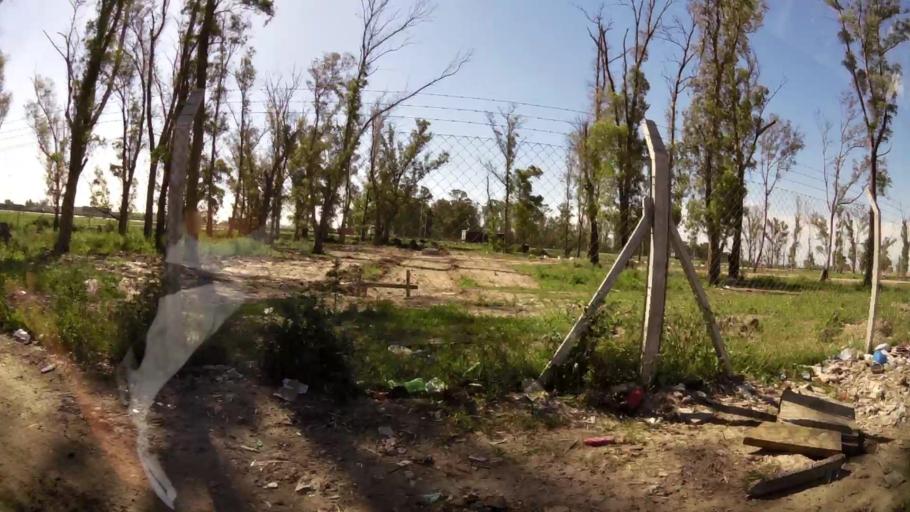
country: AR
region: Buenos Aires
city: Hurlingham
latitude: -34.5315
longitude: -58.5936
